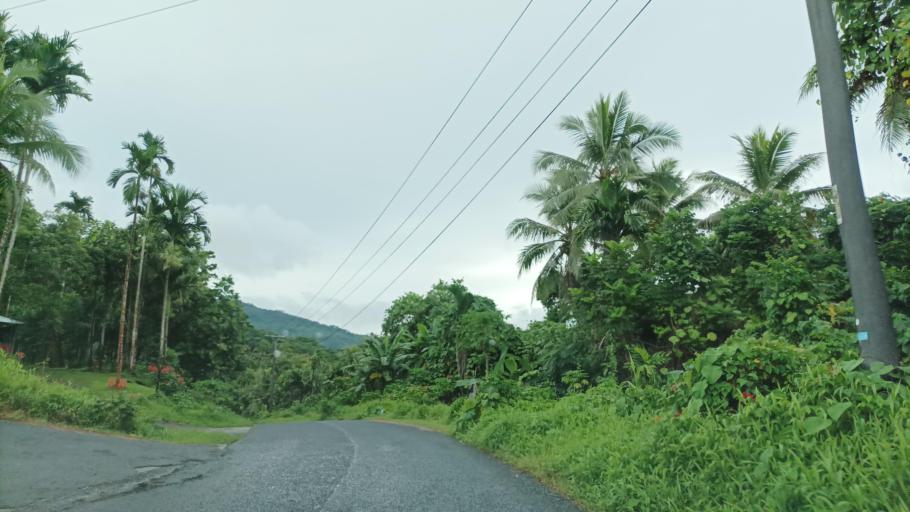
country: FM
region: Pohnpei
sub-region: Sokehs Municipality
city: Palikir - National Government Center
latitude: 6.8908
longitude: 158.1535
